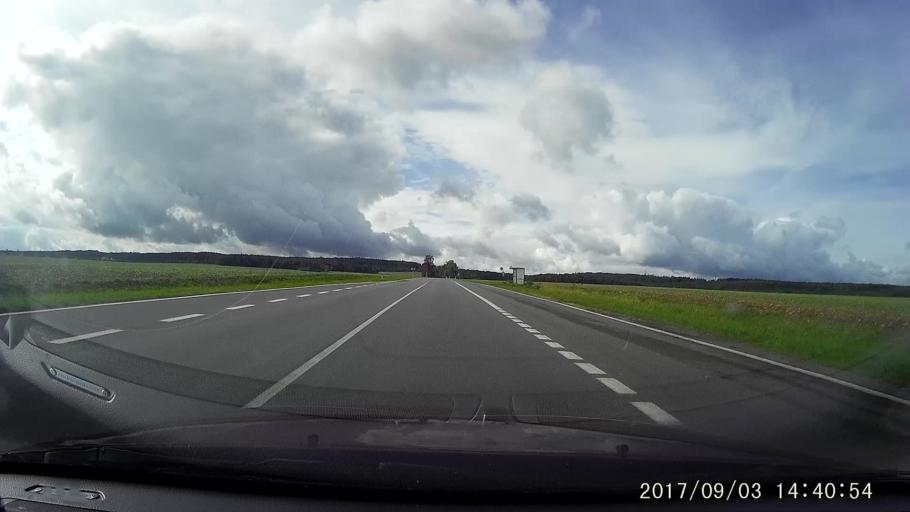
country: CZ
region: Vysocina
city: Zeletava
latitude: 49.1004
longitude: 15.7304
